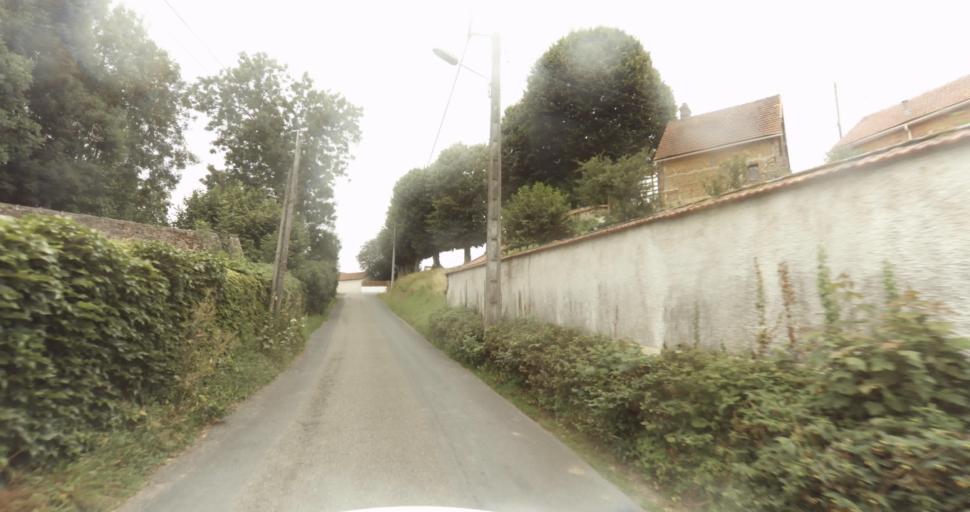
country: FR
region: Haute-Normandie
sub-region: Departement de l'Eure
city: Saint-Germain-sur-Avre
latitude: 48.7656
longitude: 1.2611
